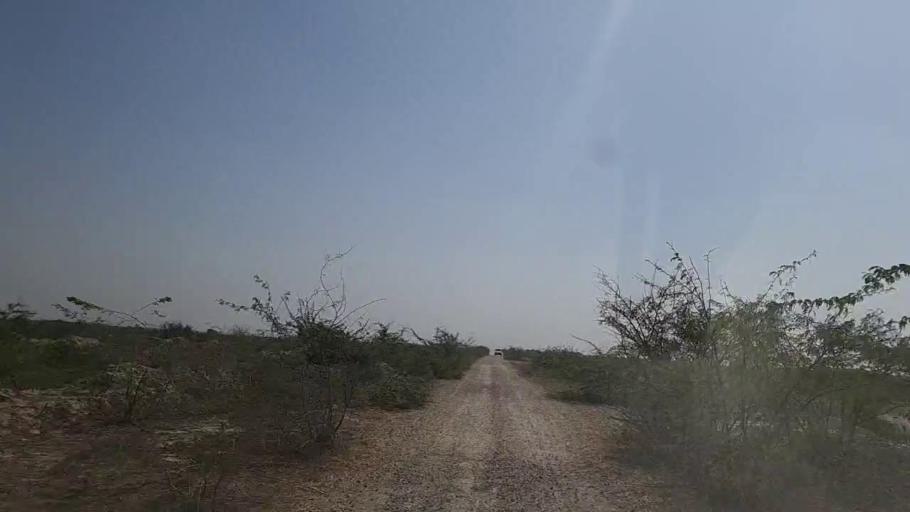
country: PK
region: Sindh
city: Naukot
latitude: 24.6379
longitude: 69.2735
